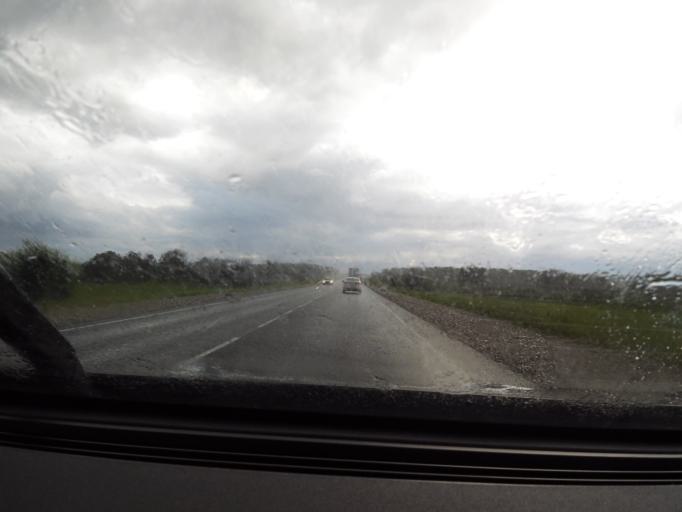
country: RU
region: Tatarstan
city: Nizhniye Vyazovyye
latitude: 55.7252
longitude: 48.4929
